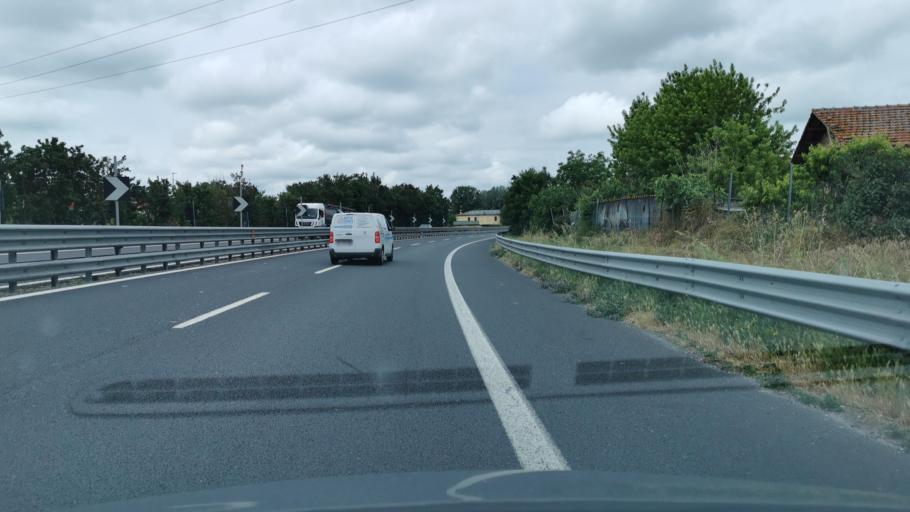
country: IT
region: Emilia-Romagna
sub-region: Provincia di Ravenna
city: Fornace Zarattini
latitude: 44.4176
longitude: 12.1357
